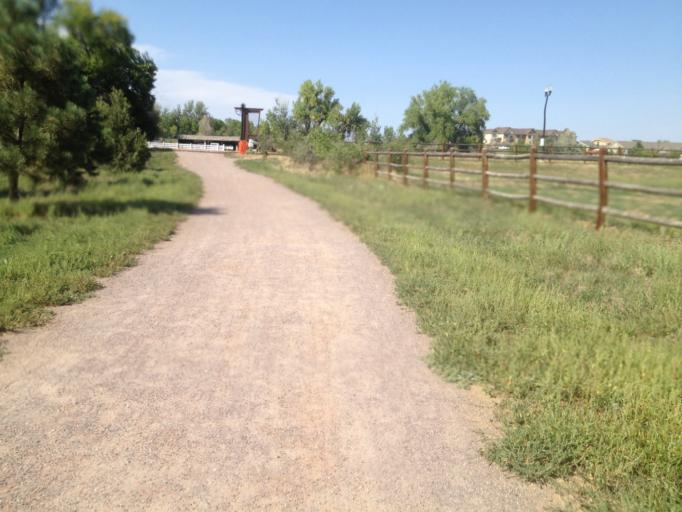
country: US
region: Colorado
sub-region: Boulder County
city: Lafayette
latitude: 39.9995
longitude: -105.1110
